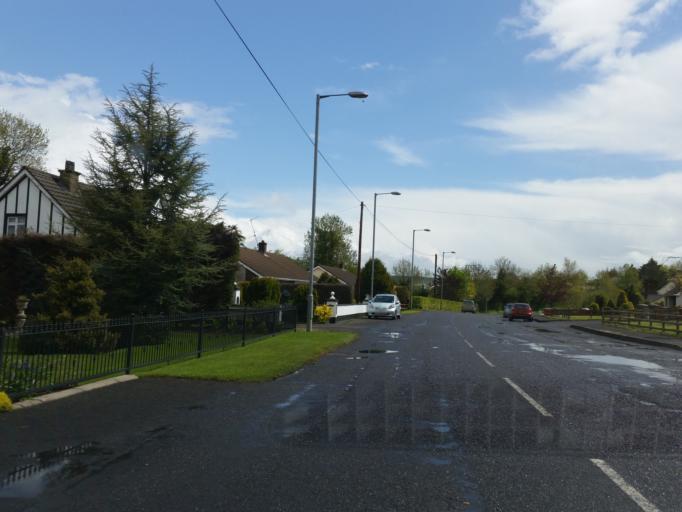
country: GB
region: Northern Ireland
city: Lisnaskea
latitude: 54.2968
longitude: -7.4714
